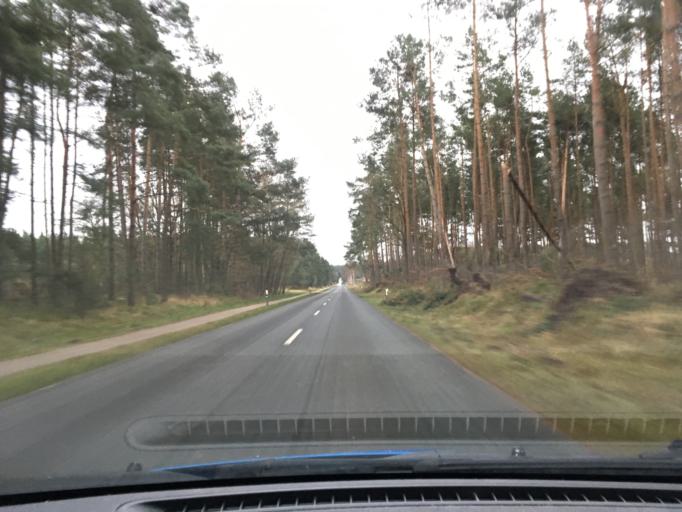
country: DE
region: Lower Saxony
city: Bleckede
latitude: 53.2713
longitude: 10.7831
